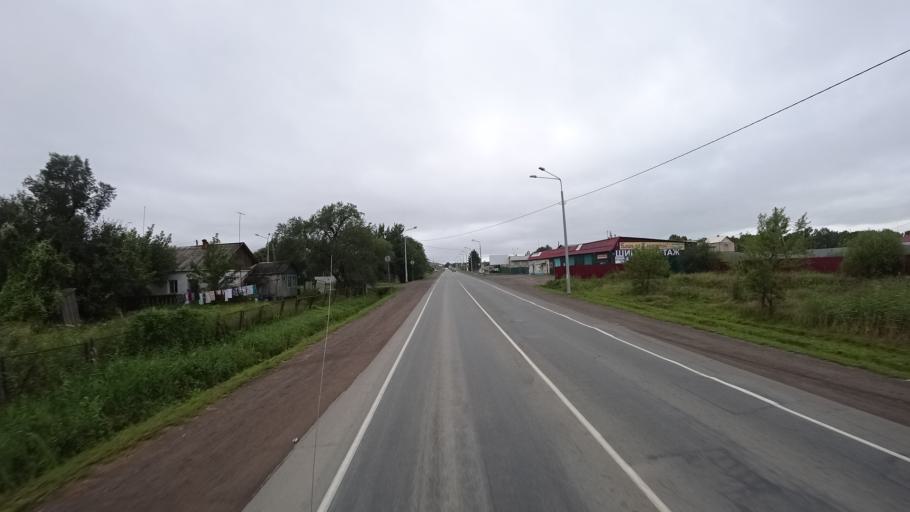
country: RU
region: Primorskiy
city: Chernigovka
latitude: 44.3319
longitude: 132.5775
